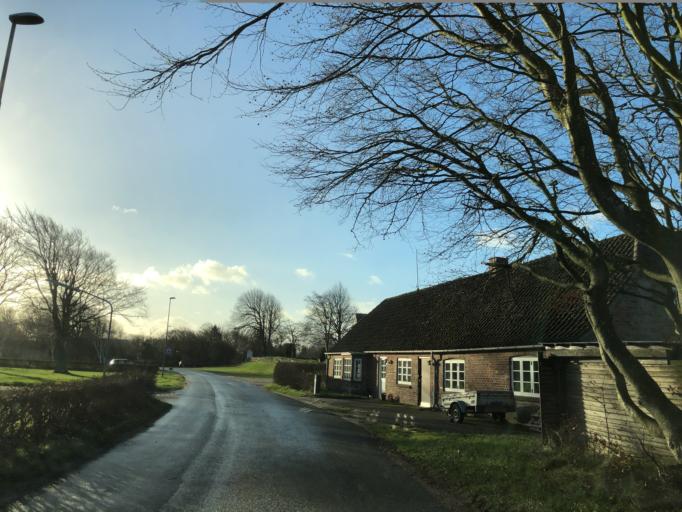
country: DK
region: Central Jutland
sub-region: Holstebro Kommune
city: Ulfborg
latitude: 56.2077
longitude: 8.2569
